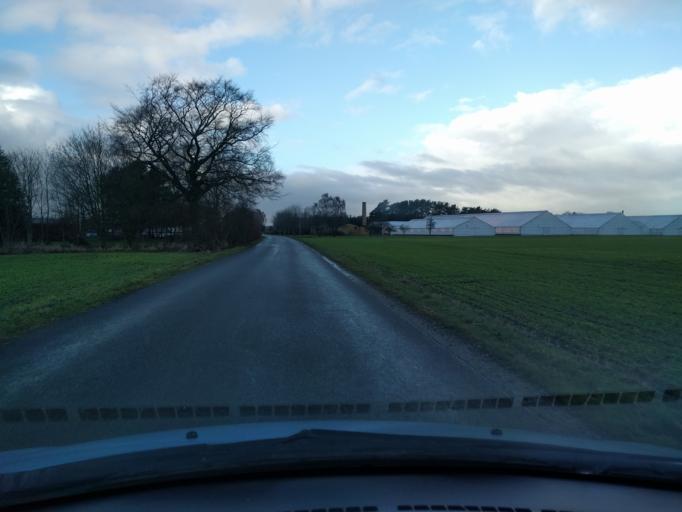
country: DK
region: South Denmark
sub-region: Kerteminde Kommune
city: Langeskov
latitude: 55.3946
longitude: 10.5585
